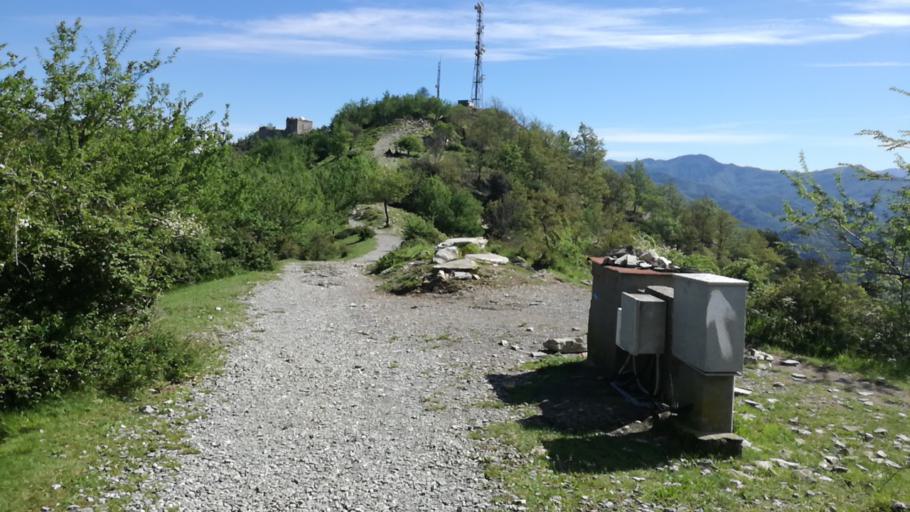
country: IT
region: Liguria
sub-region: Provincia di Genova
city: Genoa
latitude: 44.4432
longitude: 8.9330
